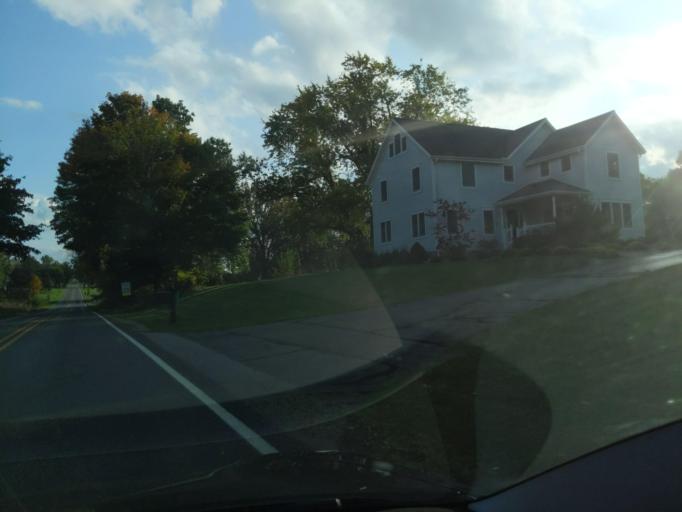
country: US
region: Michigan
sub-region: Jackson County
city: Jackson
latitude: 42.3359
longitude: -84.4629
